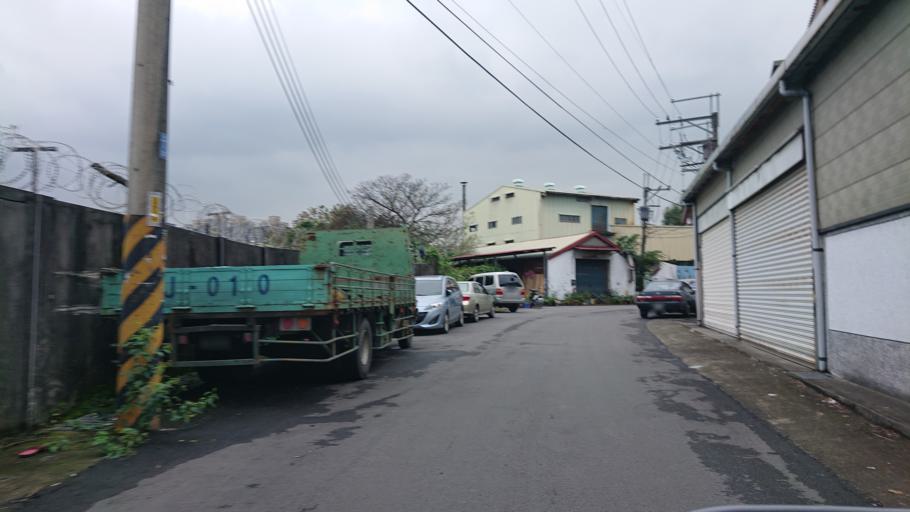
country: TW
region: Taiwan
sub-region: Taoyuan
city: Taoyuan
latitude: 24.9443
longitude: 121.3901
